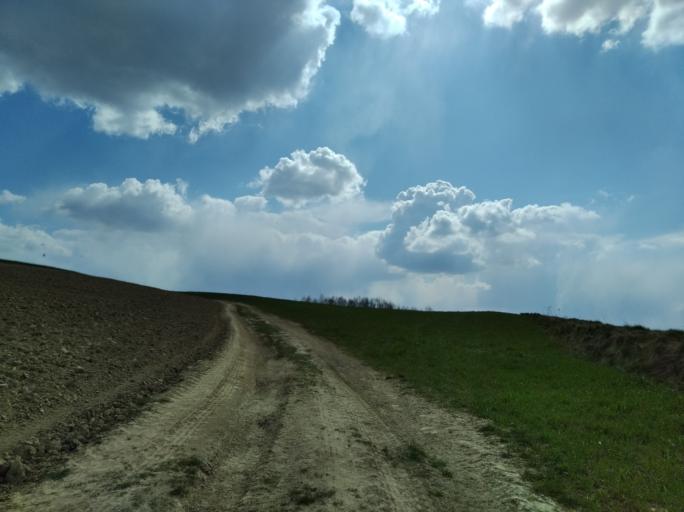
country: PL
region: Subcarpathian Voivodeship
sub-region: Powiat strzyzowski
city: Strzyzow
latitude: 49.9126
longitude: 21.7478
